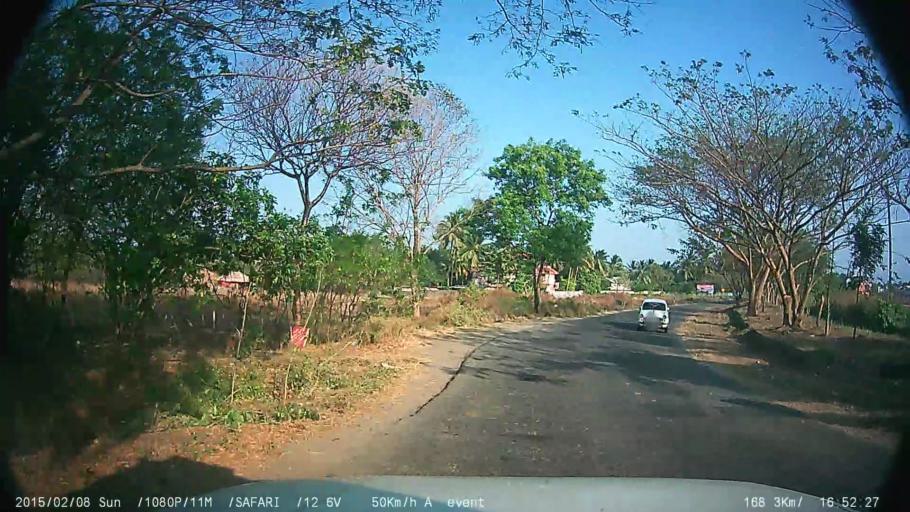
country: IN
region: Kerala
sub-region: Palakkad district
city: Palakkad
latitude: 10.7479
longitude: 76.6478
